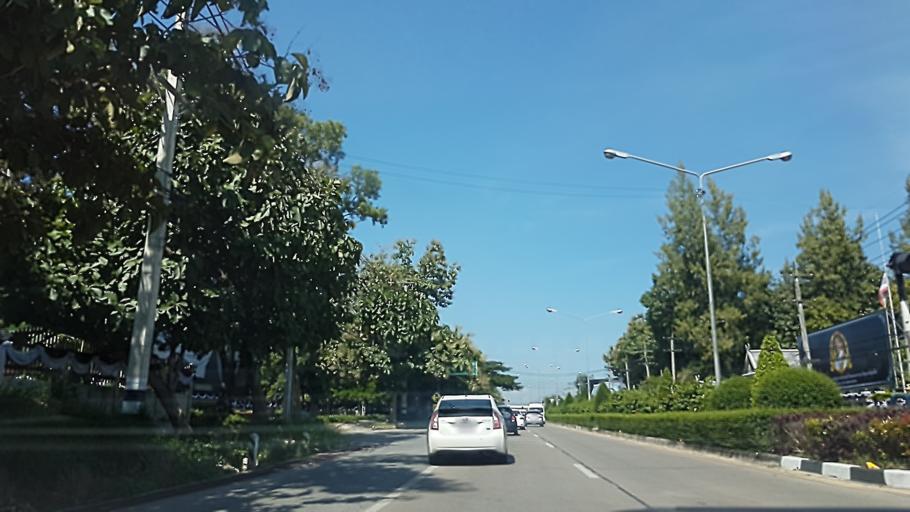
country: TH
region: Chiang Mai
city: Chiang Mai
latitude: 18.8377
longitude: 98.9746
